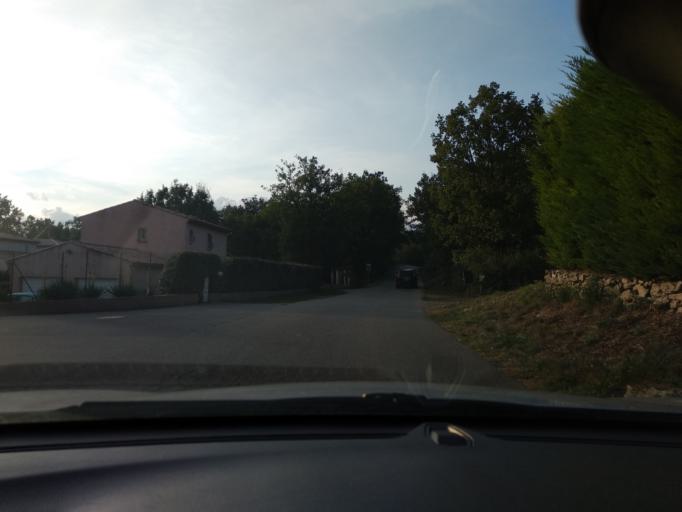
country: FR
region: Provence-Alpes-Cote d'Azur
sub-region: Departement des Alpes-Maritimes
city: Saint-Cezaire-sur-Siagne
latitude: 43.6542
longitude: 6.8109
